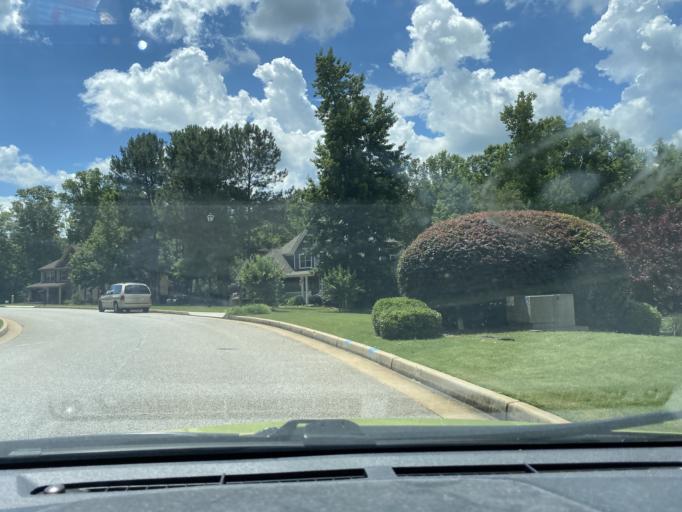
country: US
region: Georgia
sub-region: Fayette County
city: Peachtree City
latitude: 33.4255
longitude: -84.6697
